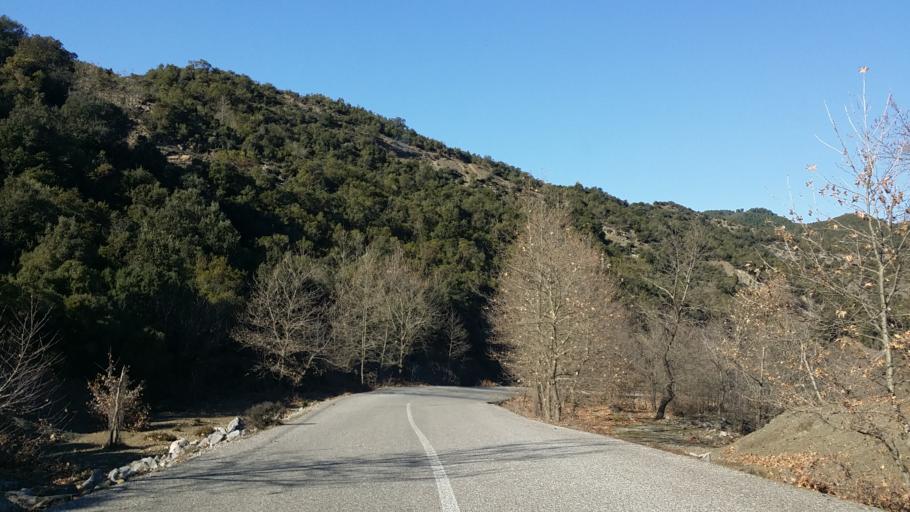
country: GR
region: Central Greece
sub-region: Nomos Evrytanias
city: Kerasochori
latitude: 38.9946
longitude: 21.5143
